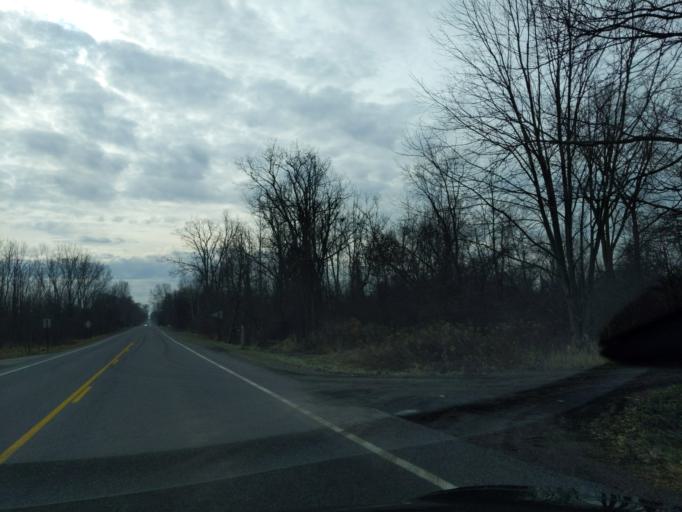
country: US
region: Michigan
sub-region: Ingham County
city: Holt
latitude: 42.5742
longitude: -84.5228
